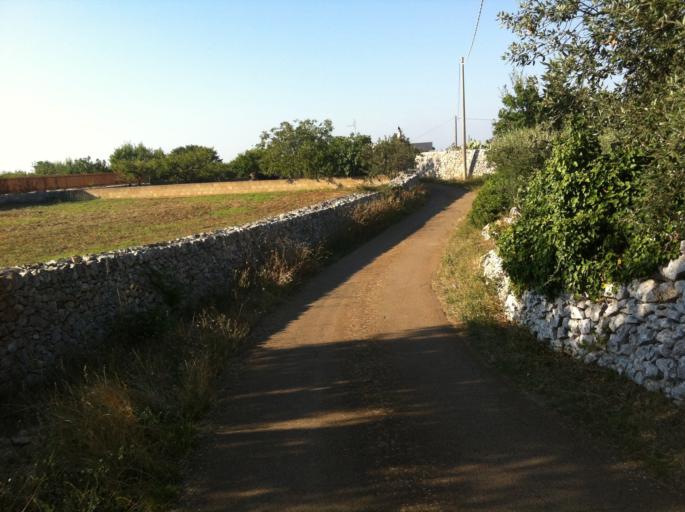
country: IT
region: Apulia
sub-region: Provincia di Bari
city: Putignano
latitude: 40.8245
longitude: 17.1391
